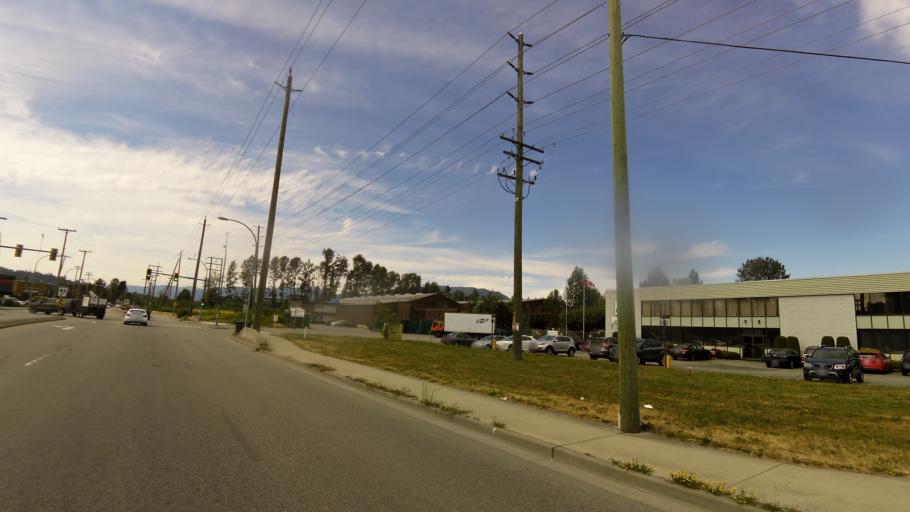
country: CA
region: British Columbia
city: Coquitlam
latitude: 49.2533
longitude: -122.7632
